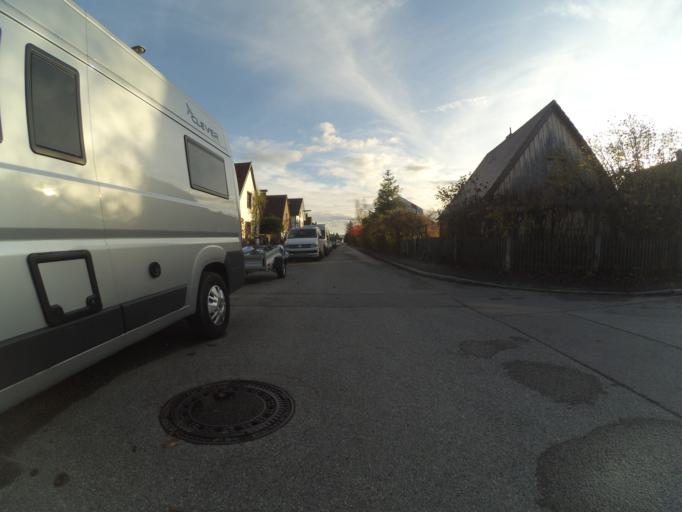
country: DE
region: Bavaria
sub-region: Upper Bavaria
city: Bogenhausen
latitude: 48.1974
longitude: 11.5885
